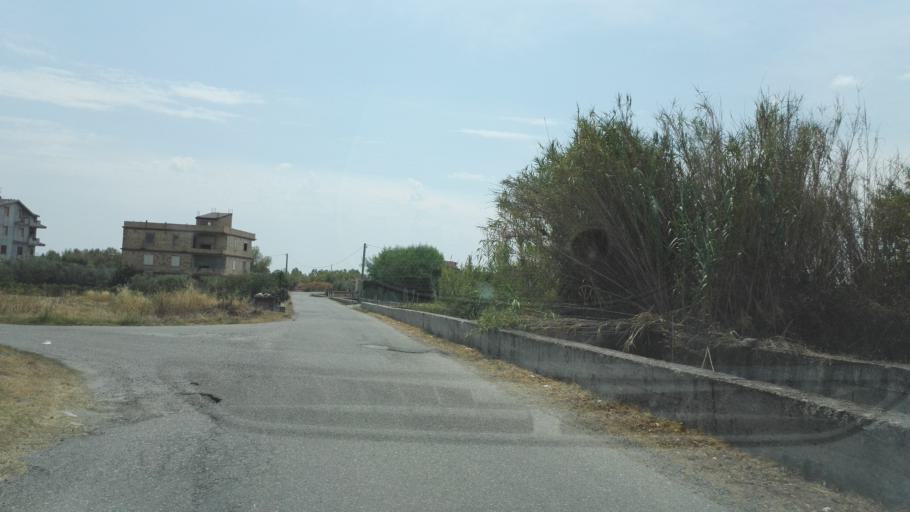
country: IT
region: Calabria
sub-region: Provincia di Reggio Calabria
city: Monasterace Marina
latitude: 38.4327
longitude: 16.5580
